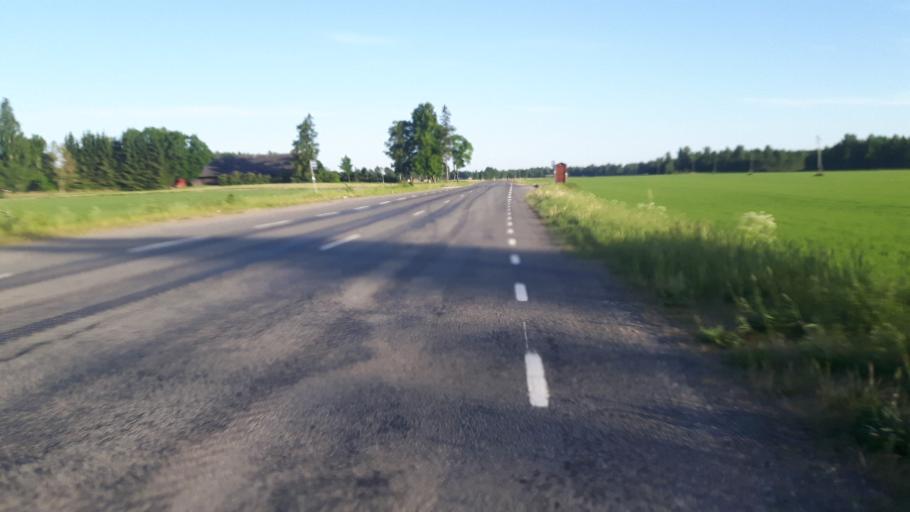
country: EE
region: Raplamaa
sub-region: Jaervakandi vald
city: Jarvakandi
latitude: 58.7784
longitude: 24.9439
